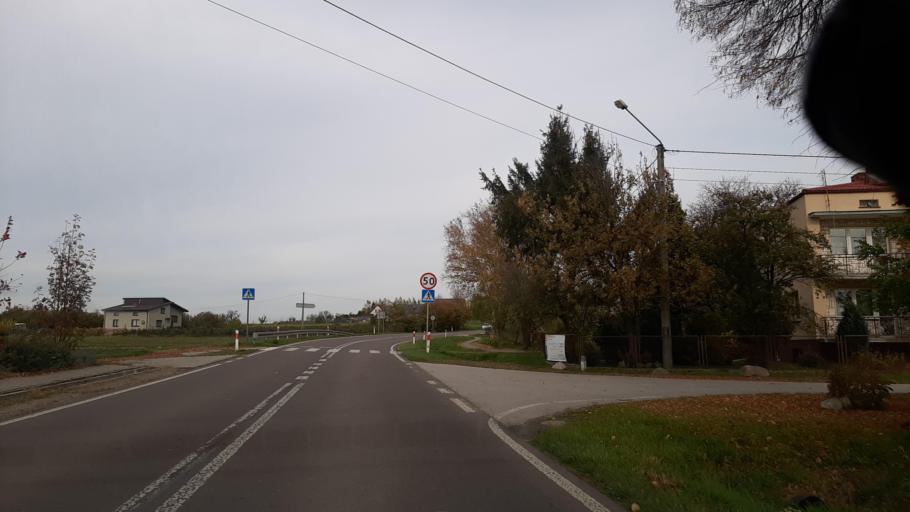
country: PL
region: Lublin Voivodeship
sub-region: Powiat pulawski
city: Markuszow
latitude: 51.3654
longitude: 22.2791
